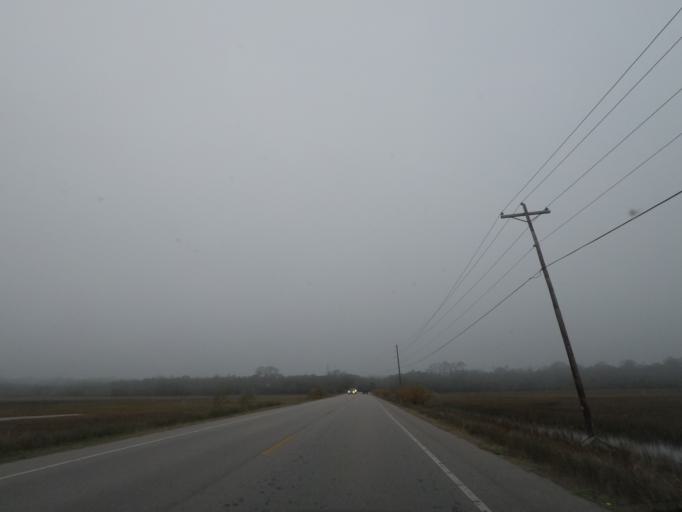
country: US
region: South Carolina
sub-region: Charleston County
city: Seabrook Island
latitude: 32.5068
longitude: -80.2985
